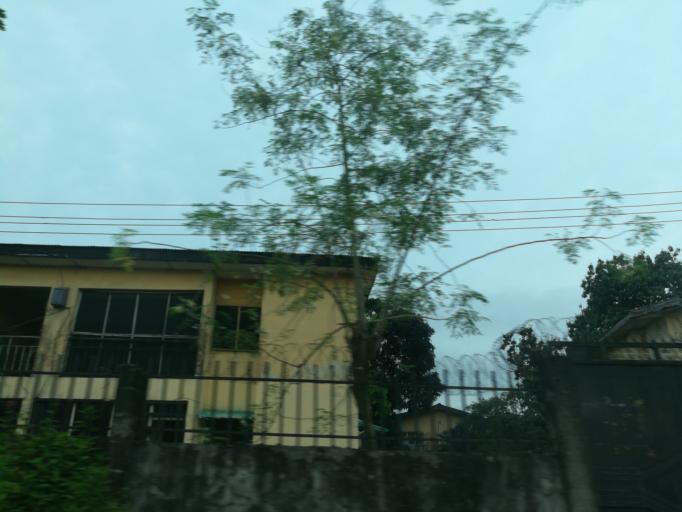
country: NG
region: Rivers
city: Port Harcourt
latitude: 4.8210
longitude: 7.0267
